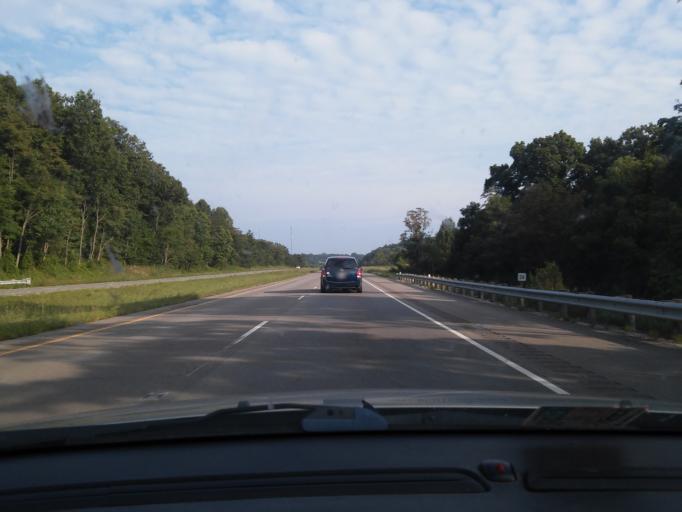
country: US
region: Ohio
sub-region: Jackson County
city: Oak Hill
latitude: 38.9435
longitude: -82.4748
